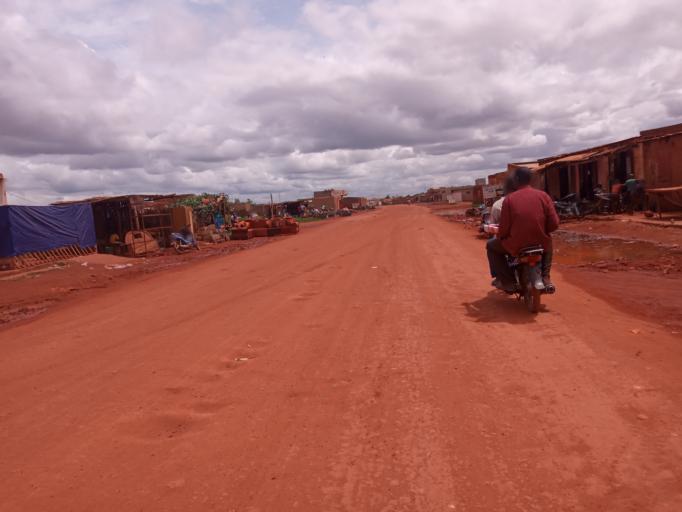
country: ML
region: Bamako
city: Bamako
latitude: 12.5350
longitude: -7.9943
